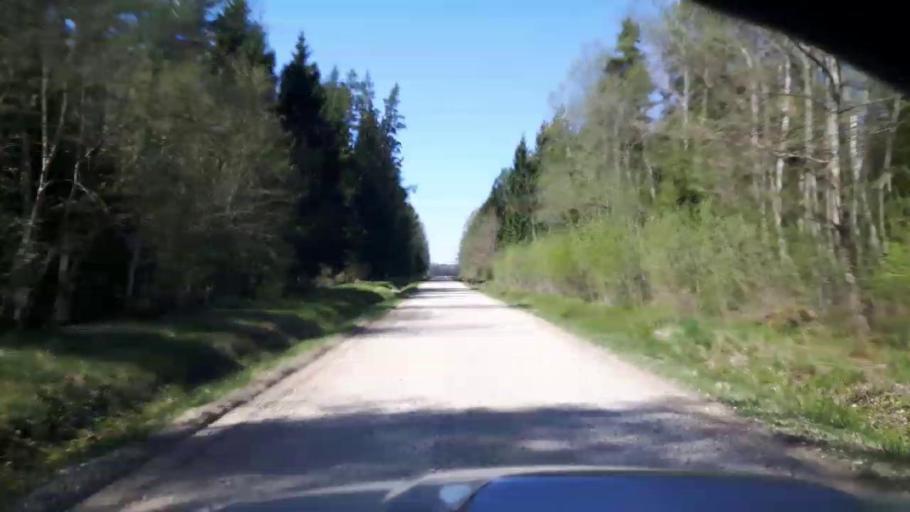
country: EE
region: Paernumaa
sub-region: Tootsi vald
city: Tootsi
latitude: 58.4737
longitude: 24.7559
